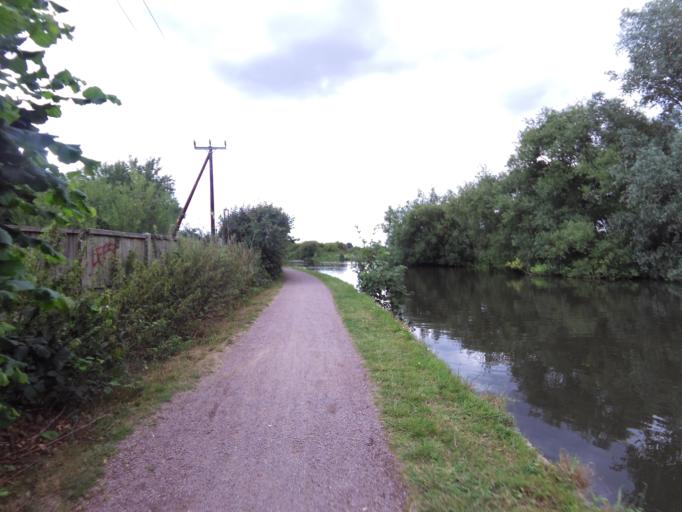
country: GB
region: England
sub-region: Hertfordshire
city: Broxbourne
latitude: 51.7329
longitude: -0.0132
